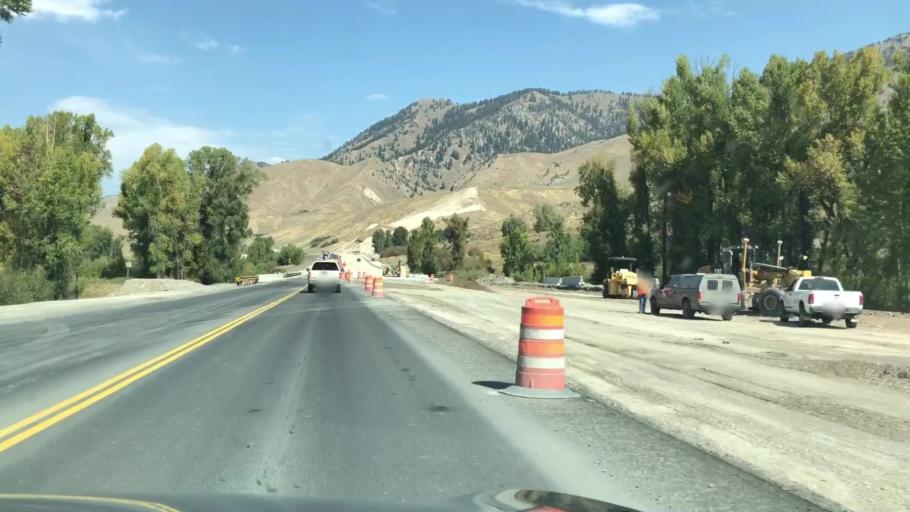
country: US
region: Wyoming
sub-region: Teton County
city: South Park
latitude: 43.3874
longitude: -110.7467
